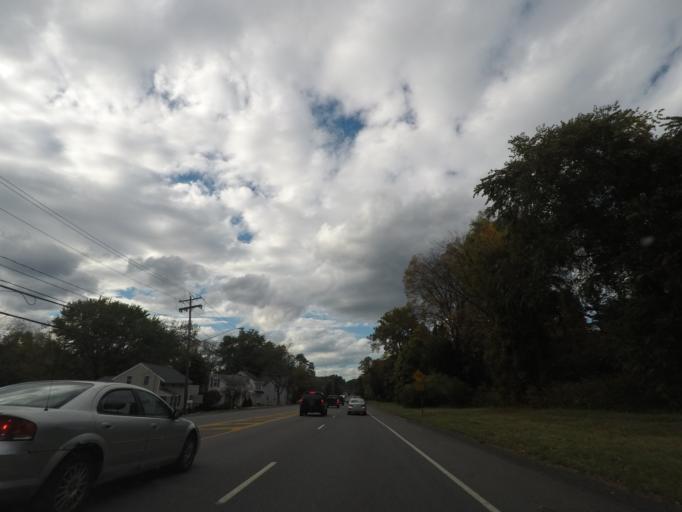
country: US
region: New York
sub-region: Albany County
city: Westmere
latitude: 42.7015
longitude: -73.9049
